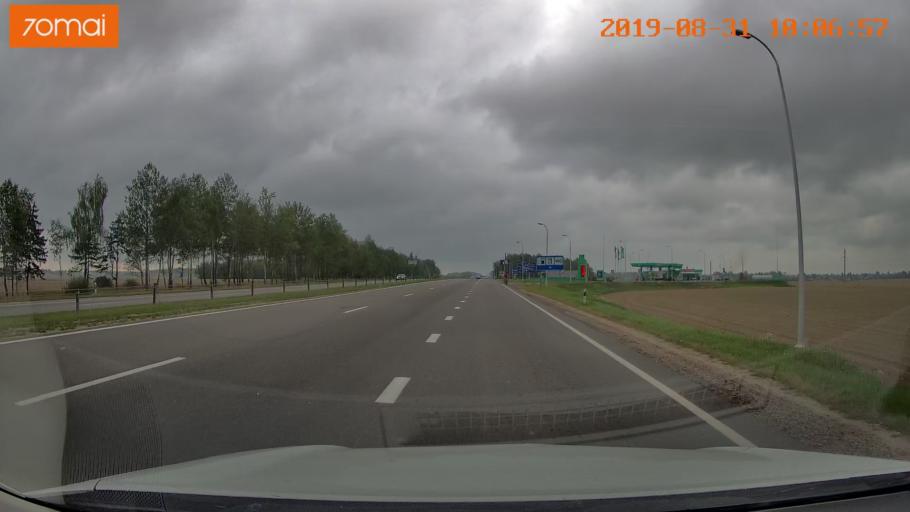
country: BY
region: Mogilev
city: Buynichy
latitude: 53.9541
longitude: 30.2104
